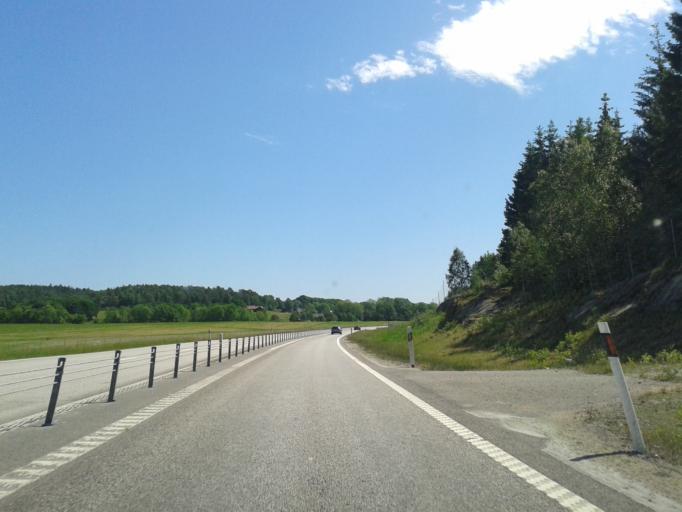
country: SE
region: Vaestra Goetaland
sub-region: Orust
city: Henan
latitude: 58.3513
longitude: 11.7364
